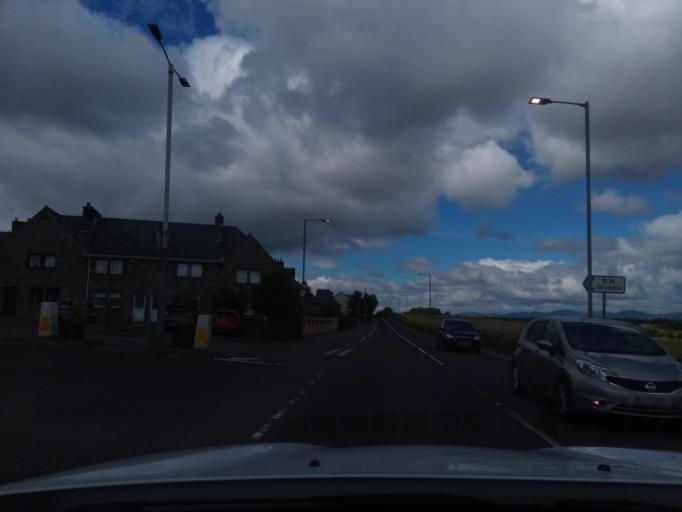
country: GB
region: Scotland
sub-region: Fife
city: Cairneyhill
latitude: 56.0492
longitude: -3.5273
